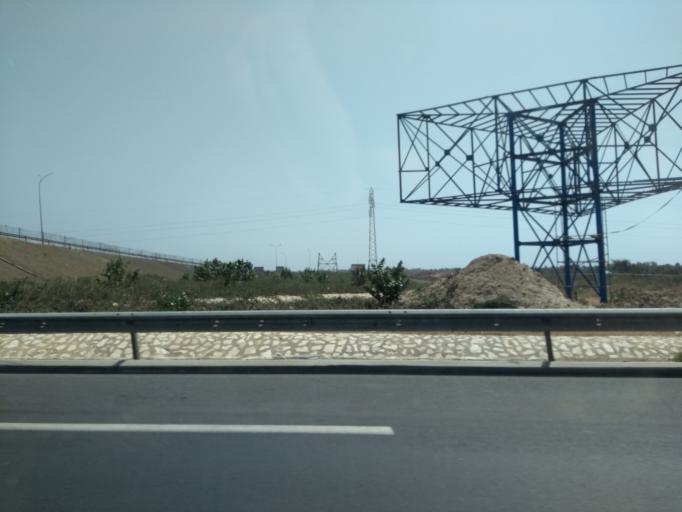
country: SN
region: Dakar
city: Pikine
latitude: 14.7564
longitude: -17.3228
